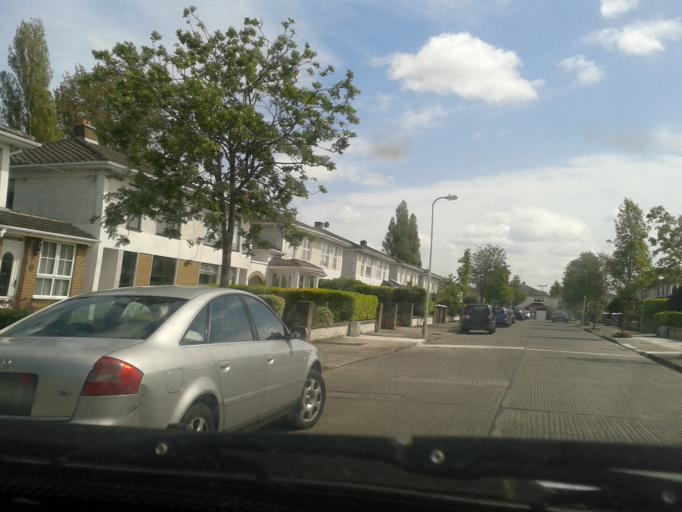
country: IE
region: Leinster
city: Glasnevin
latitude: 53.3788
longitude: -6.2564
